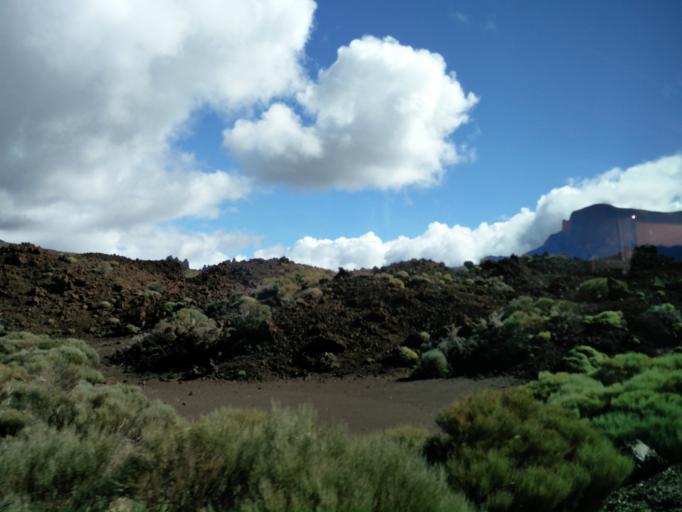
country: ES
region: Canary Islands
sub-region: Provincia de Santa Cruz de Tenerife
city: Vilaflor
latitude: 28.2139
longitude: -16.6640
